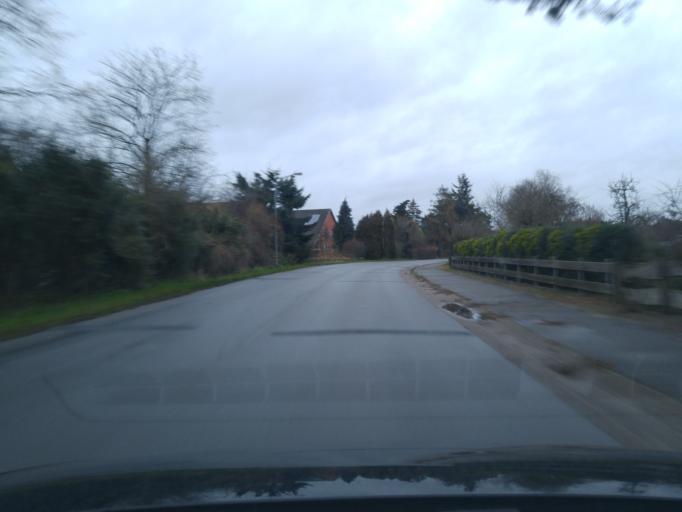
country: DE
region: Lower Saxony
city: Scharnebeck
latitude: 53.2961
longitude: 10.5066
